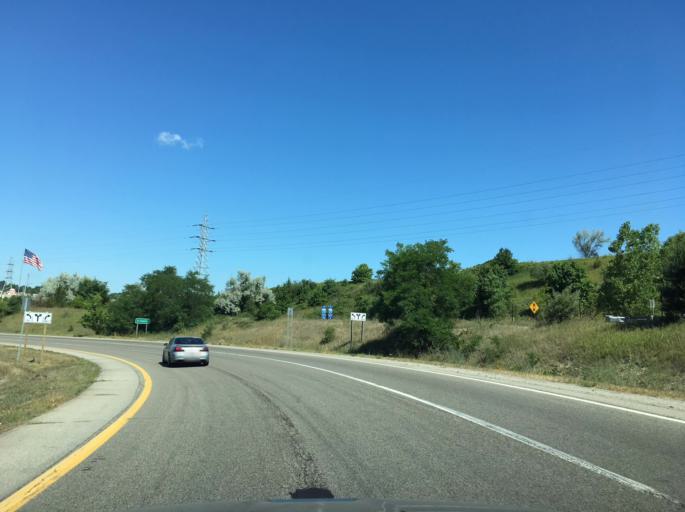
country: US
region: Michigan
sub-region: Oakland County
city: Auburn Hills
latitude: 42.7026
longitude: -83.2826
